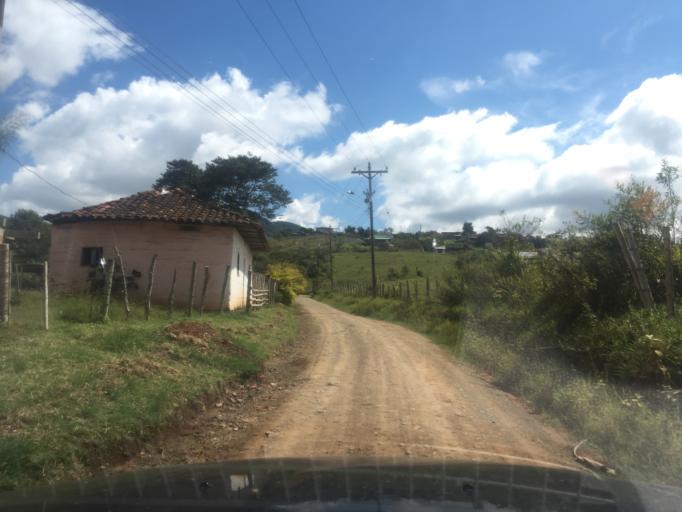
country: CO
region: Valle del Cauca
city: Yumbo
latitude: 3.6627
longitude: -76.5600
